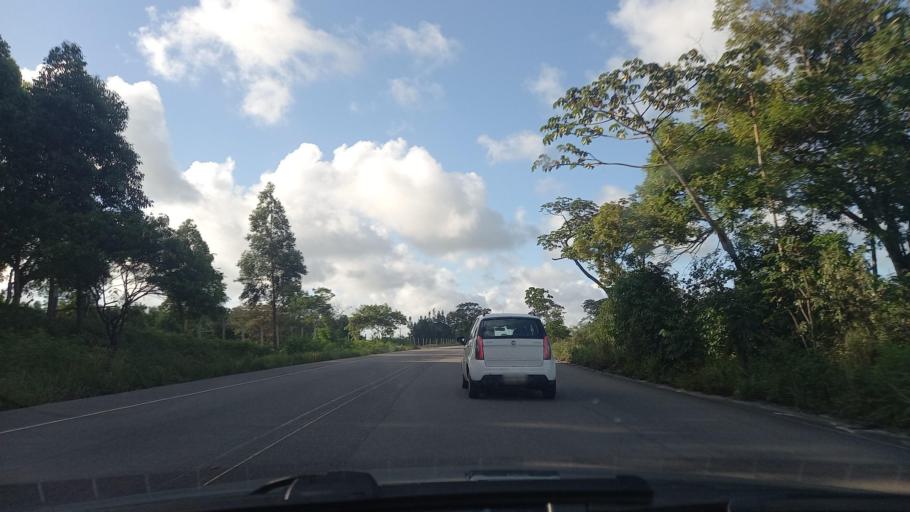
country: BR
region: Alagoas
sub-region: Marechal Deodoro
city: Marechal Deodoro
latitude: -9.8300
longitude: -35.9293
